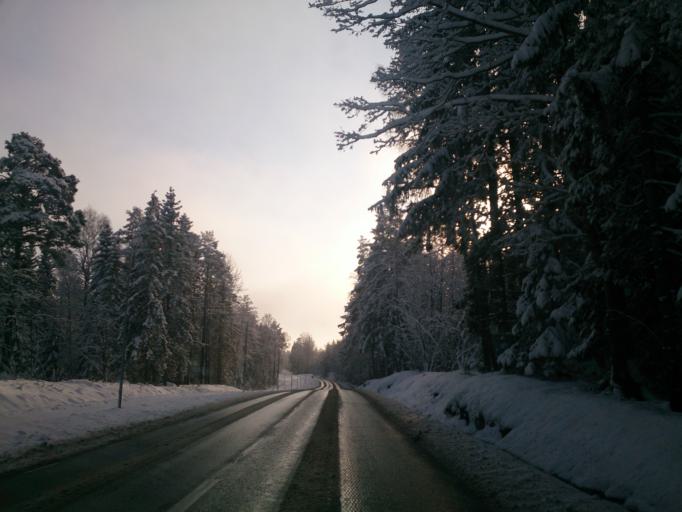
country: SE
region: Stockholm
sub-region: Varmdo Kommun
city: Hemmesta
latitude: 59.2939
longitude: 18.5190
